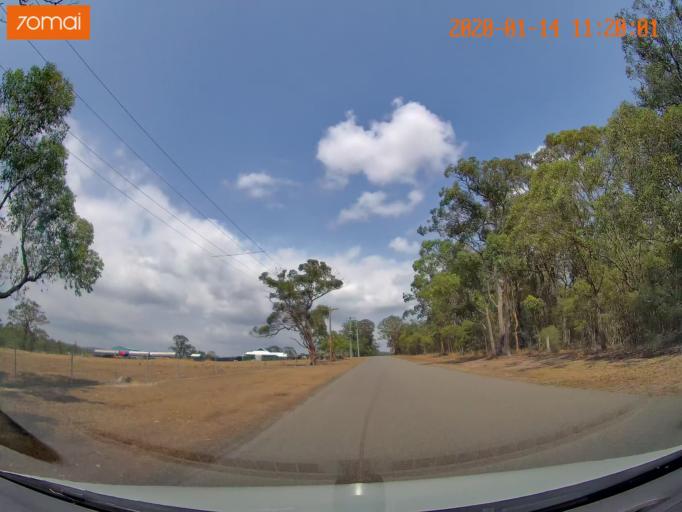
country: AU
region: New South Wales
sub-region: Lake Macquarie Shire
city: Cooranbong
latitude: -33.1004
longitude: 151.4584
